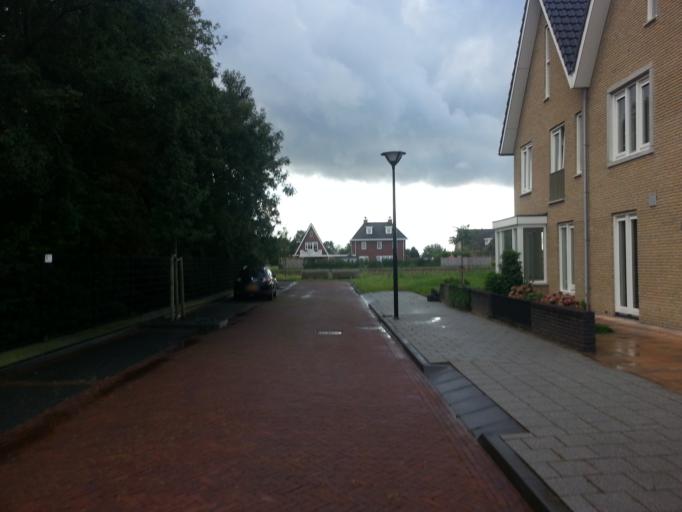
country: NL
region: South Holland
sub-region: Gemeente Spijkenisse
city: Spijkenisse
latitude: 51.8264
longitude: 4.2511
